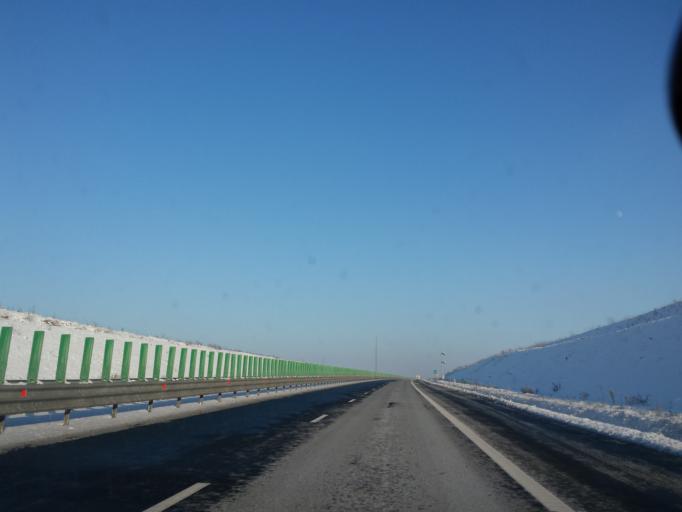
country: RO
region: Alba
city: Vurpar
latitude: 45.9589
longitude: 23.4455
